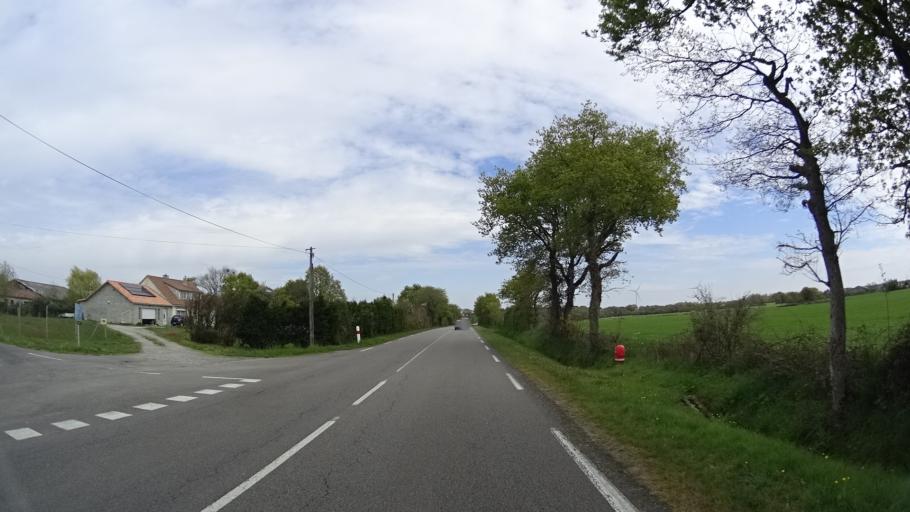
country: FR
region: Pays de la Loire
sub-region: Departement de la Loire-Atlantique
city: Chemere
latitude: 47.0694
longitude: -1.9039
